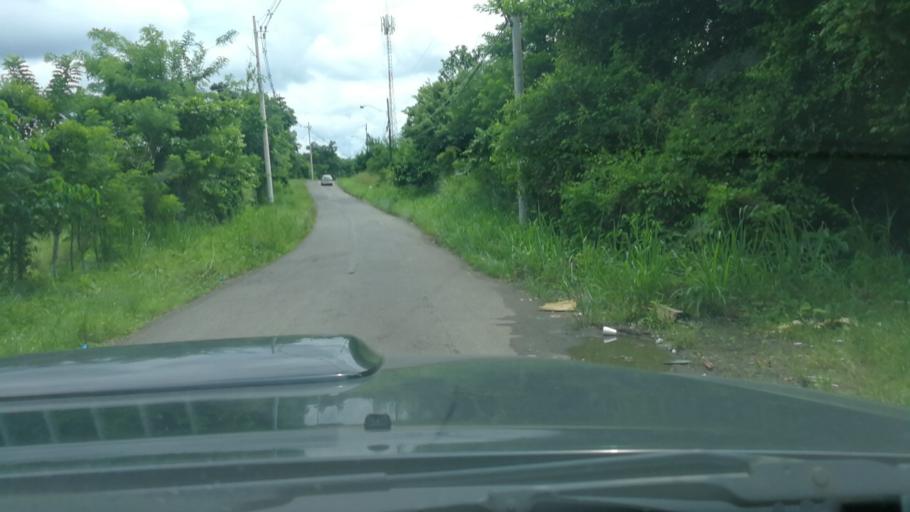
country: PA
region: Panama
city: San Miguelito
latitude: 9.1010
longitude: -79.4559
